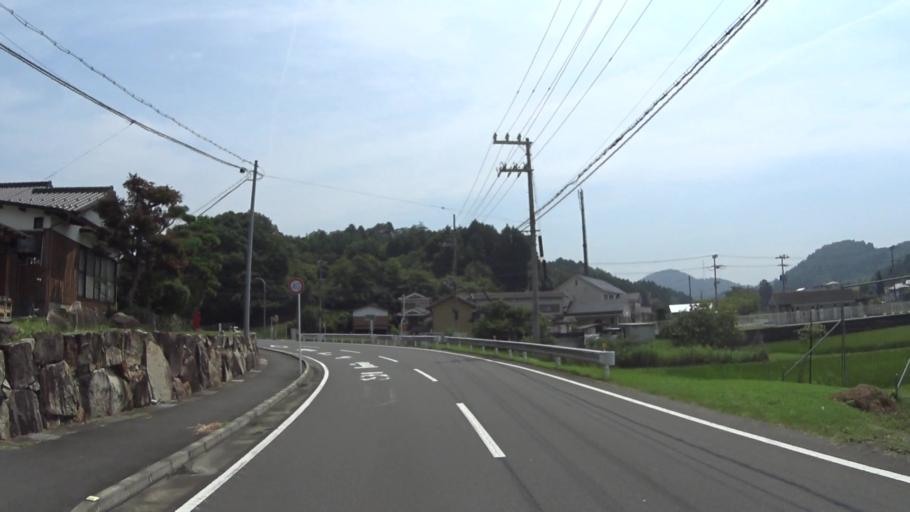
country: JP
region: Kyoto
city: Kameoka
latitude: 35.1777
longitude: 135.4430
